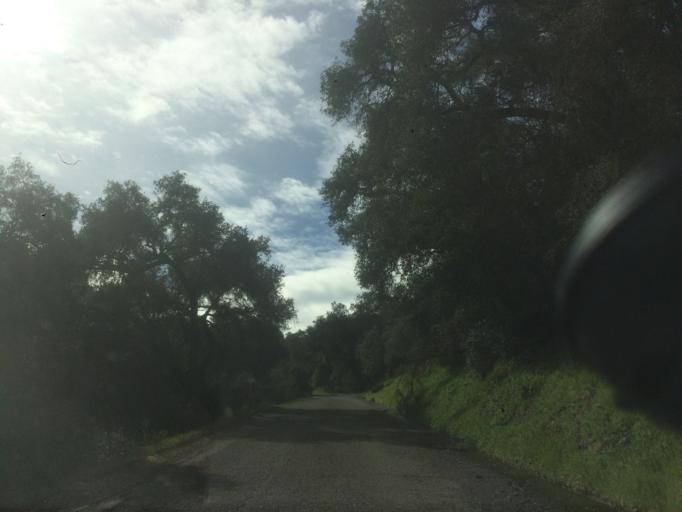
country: US
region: California
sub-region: San Luis Obispo County
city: Nipomo
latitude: 35.2127
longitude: -120.4438
